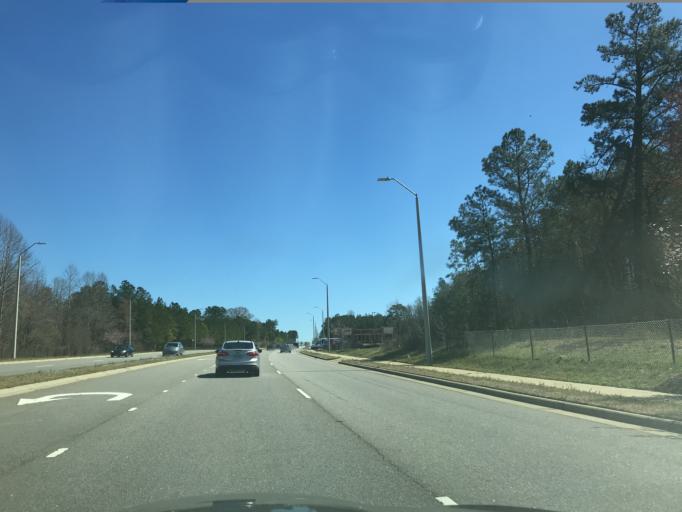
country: US
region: North Carolina
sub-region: Wake County
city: Garner
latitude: 35.6873
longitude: -78.5951
